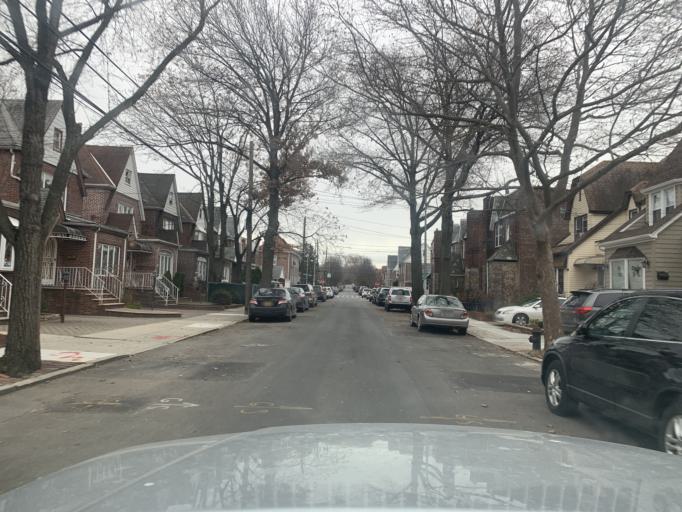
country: US
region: New York
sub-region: Queens County
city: Borough of Queens
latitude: 40.7225
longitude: -73.8706
